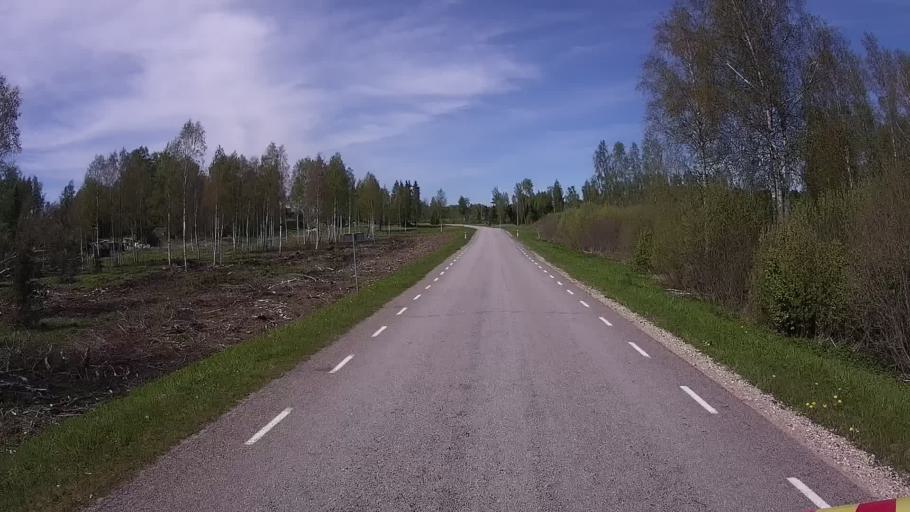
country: EE
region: Vorumaa
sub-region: Antsla vald
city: Vana-Antsla
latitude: 57.6413
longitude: 26.3305
